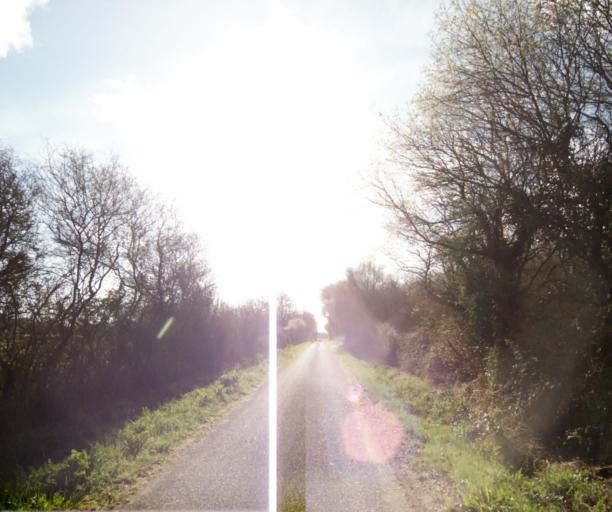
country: FR
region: Pays de la Loire
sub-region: Departement de la Loire-Atlantique
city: Bouvron
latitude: 47.4057
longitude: -1.8362
